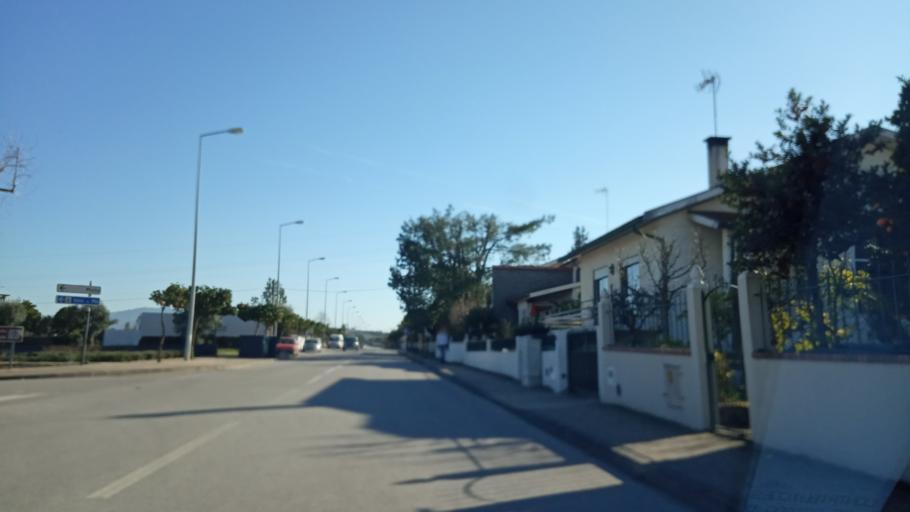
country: PT
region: Aveiro
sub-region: Anadia
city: Anadia
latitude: 40.4406
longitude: -8.4330
